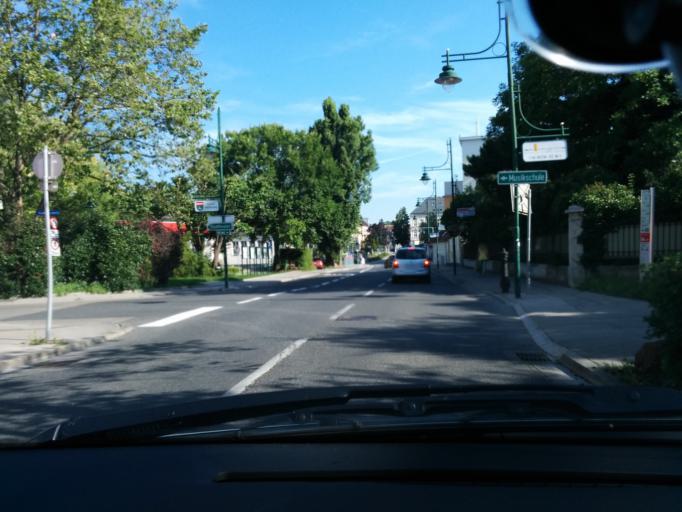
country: AT
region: Lower Austria
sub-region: Politischer Bezirk Modling
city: Modling
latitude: 48.0840
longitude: 16.2865
